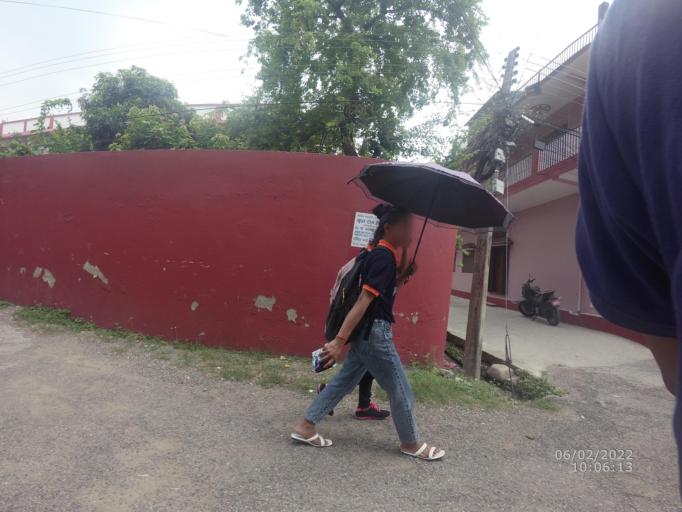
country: NP
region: Western Region
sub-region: Lumbini Zone
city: Bhairahawa
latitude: 27.5070
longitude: 83.4521
